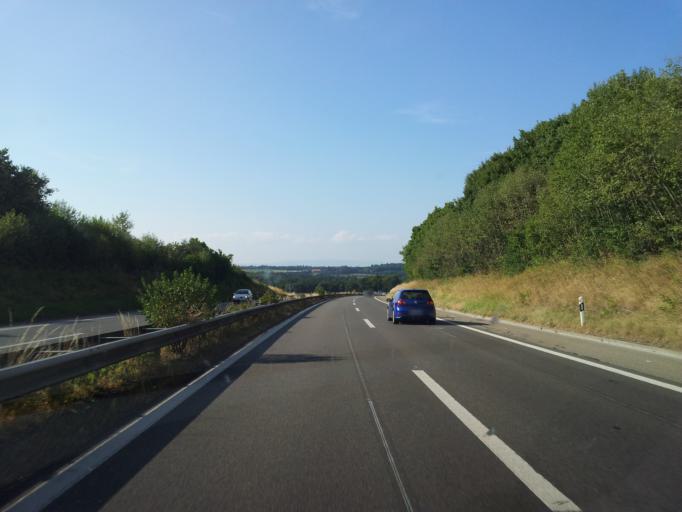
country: CH
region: Fribourg
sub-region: Sarine District
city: Matran
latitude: 46.7613
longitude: 7.0909
